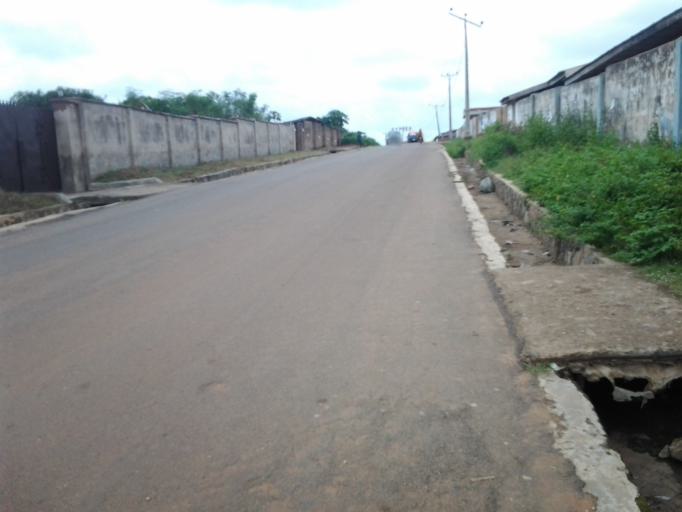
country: NG
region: Oyo
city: Ibadan
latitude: 7.4363
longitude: 3.9552
